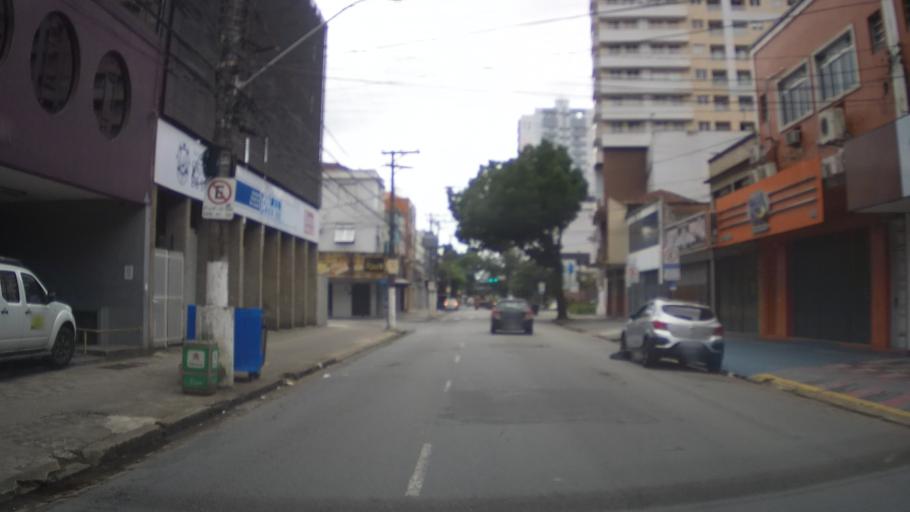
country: BR
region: Sao Paulo
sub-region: Santos
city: Santos
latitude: -23.9518
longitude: -46.3288
